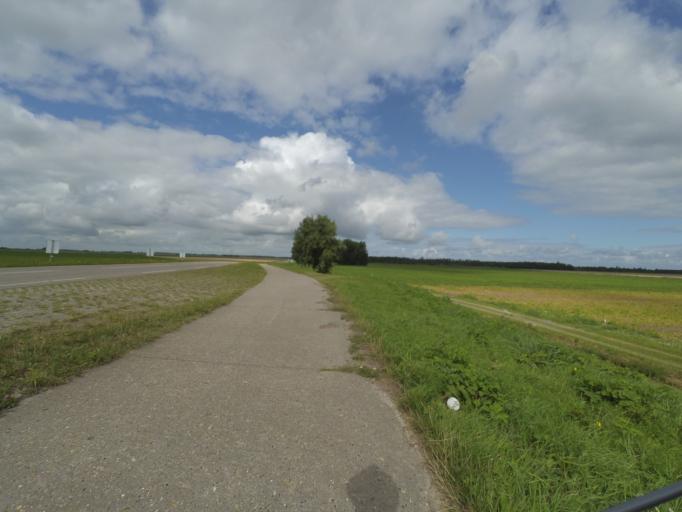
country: NL
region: Groningen
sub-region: Gemeente Zuidhorn
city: Grijpskerk
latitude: 53.3152
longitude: 6.2633
